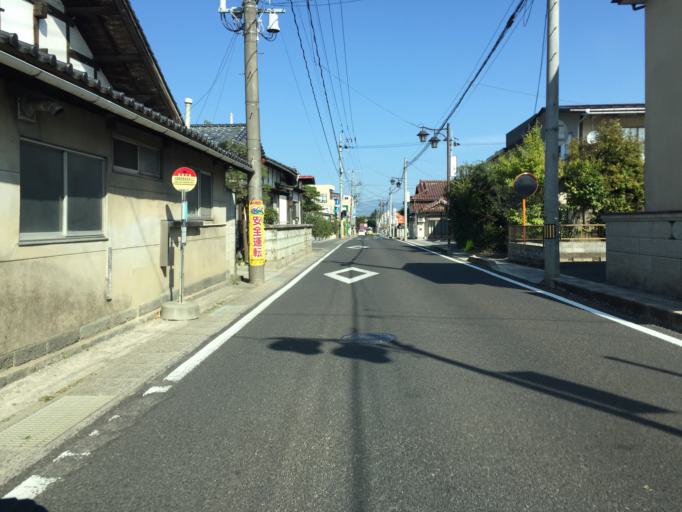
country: JP
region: Fukushima
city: Fukushima-shi
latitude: 37.7276
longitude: 140.4384
